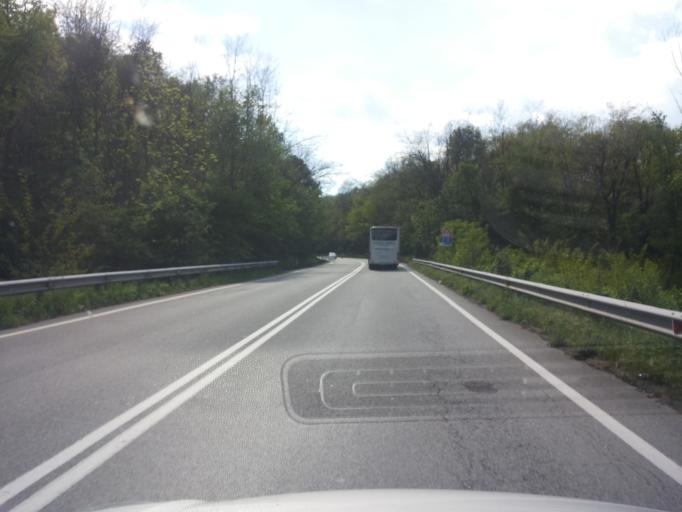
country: IT
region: Lombardy
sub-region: Provincia di Varese
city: Cantello
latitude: 45.8365
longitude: 8.9006
